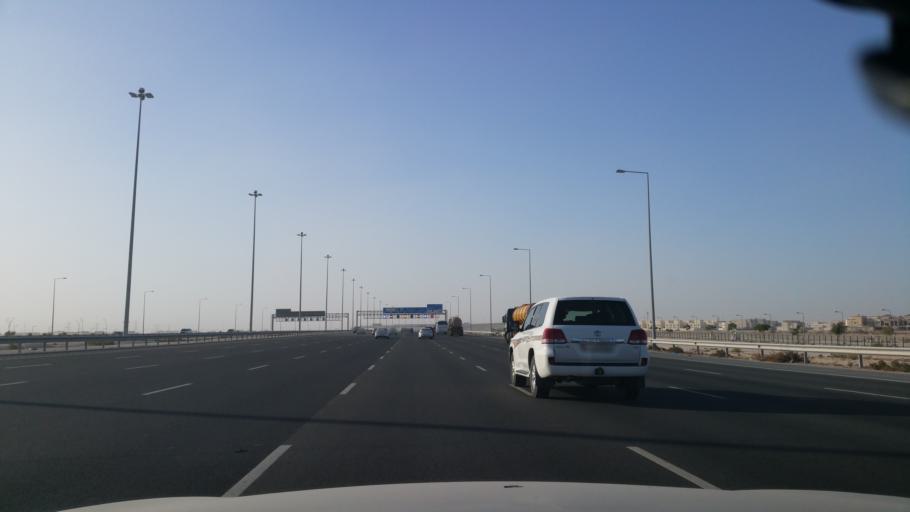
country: QA
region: Al Wakrah
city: Al Wukayr
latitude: 25.1712
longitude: 51.5588
